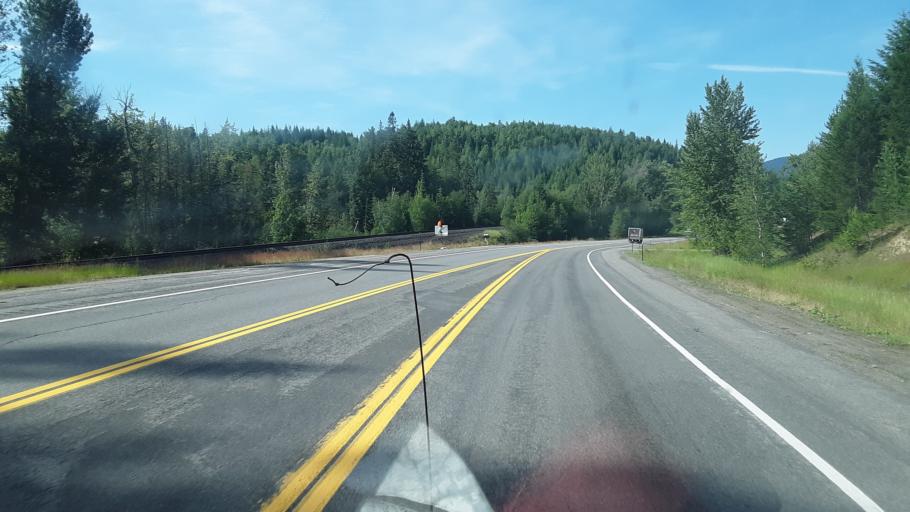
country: US
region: Idaho
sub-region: Bonner County
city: Ponderay
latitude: 48.4246
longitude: -116.4963
